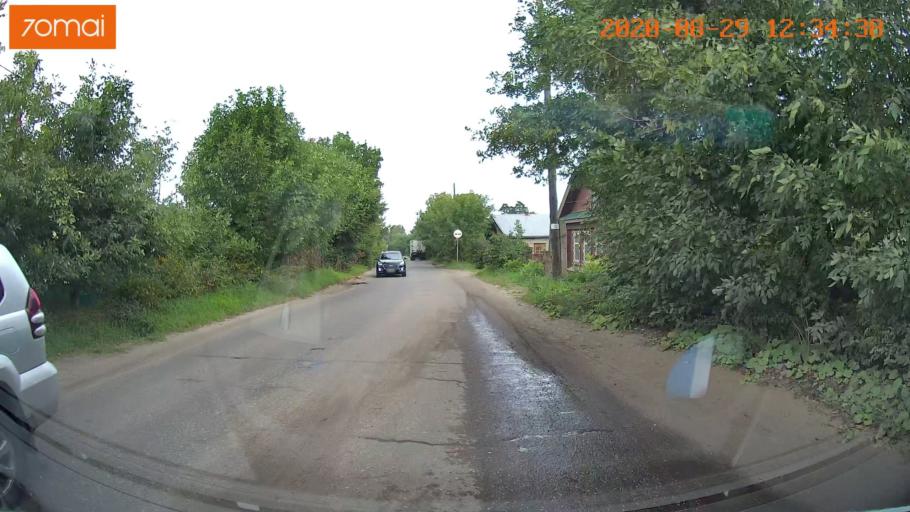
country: RU
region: Ivanovo
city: Yur'yevets
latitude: 57.3110
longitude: 43.1010
